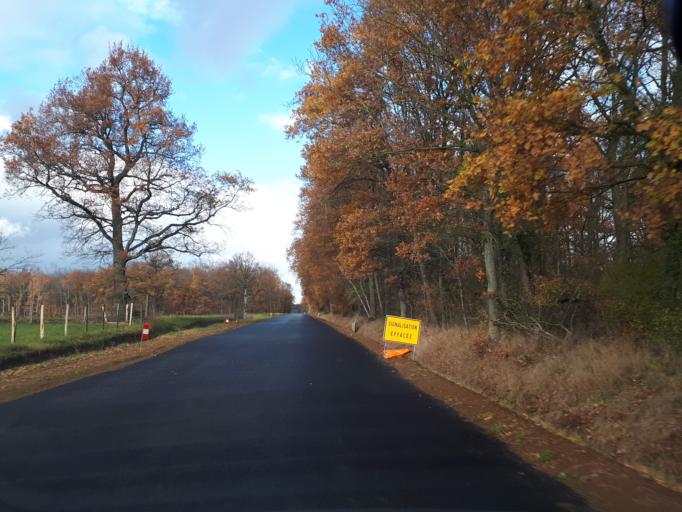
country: FR
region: Rhone-Alpes
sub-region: Departement de la Loire
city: Feurs
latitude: 45.7233
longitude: 4.2927
